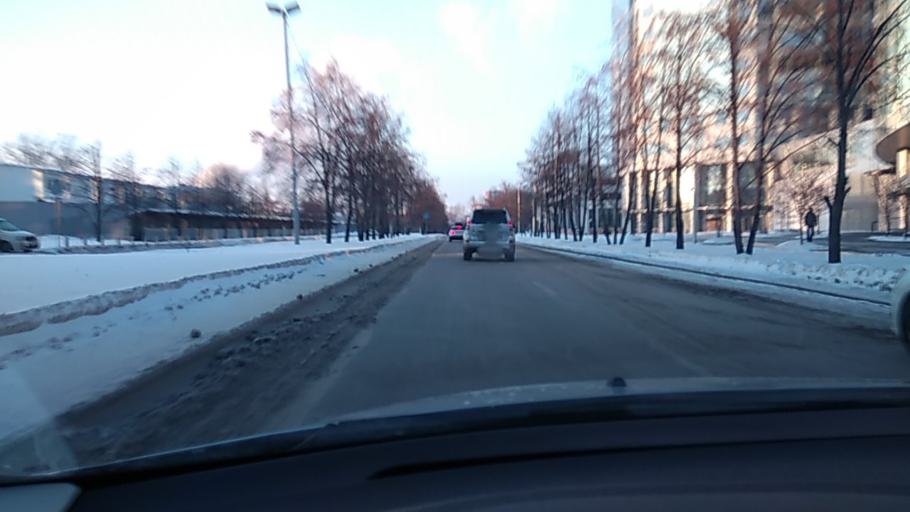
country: RU
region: Sverdlovsk
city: Yekaterinburg
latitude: 56.8441
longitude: 60.5909
